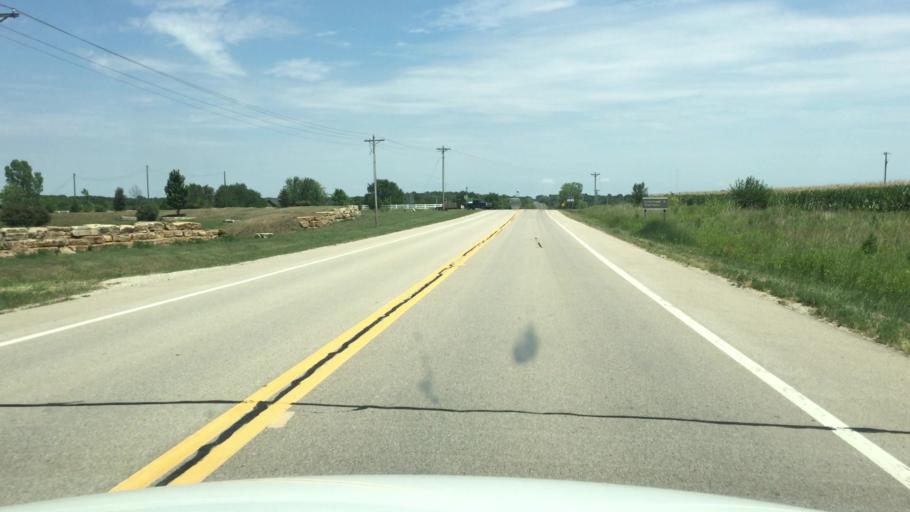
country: US
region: Kansas
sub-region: Douglas County
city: Lawrence
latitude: 38.9714
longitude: -95.4024
